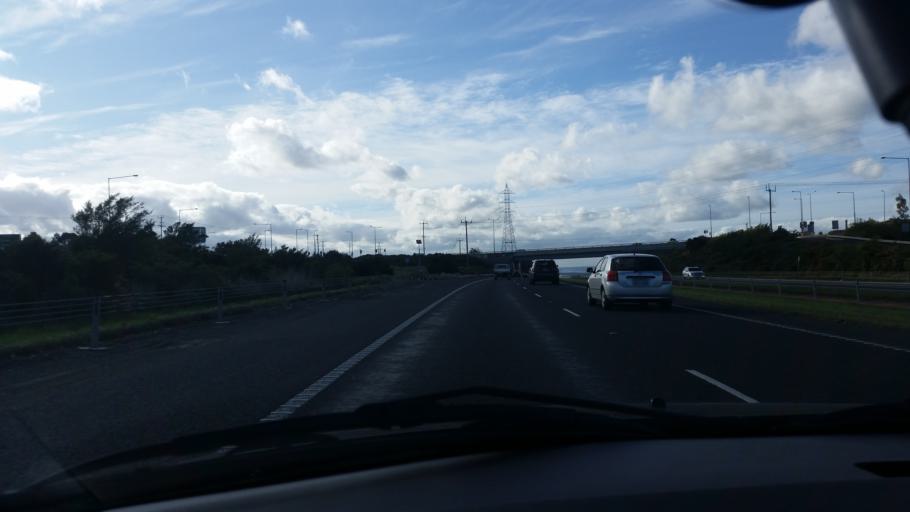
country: AU
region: Victoria
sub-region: Greater Geelong
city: Wandana Heights
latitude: -38.1744
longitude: 144.2930
